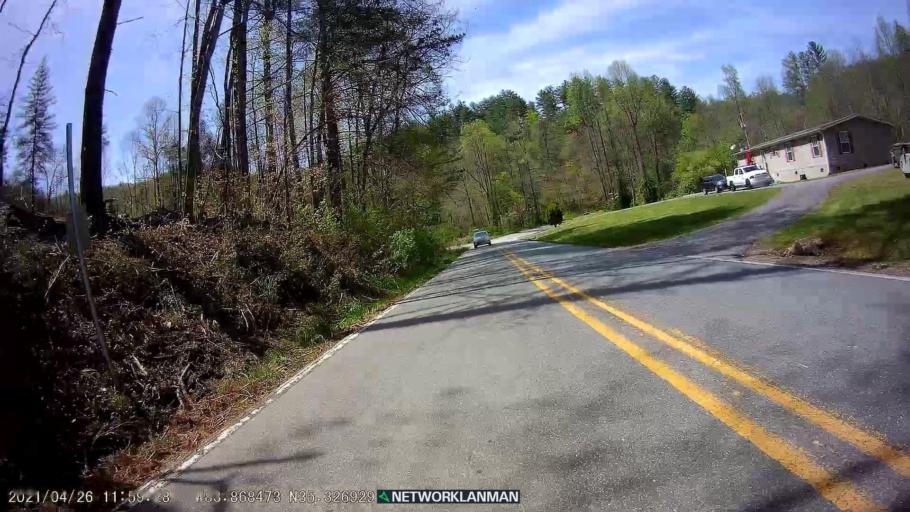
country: US
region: North Carolina
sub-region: Graham County
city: Robbinsville
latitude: 35.3268
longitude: -83.8684
